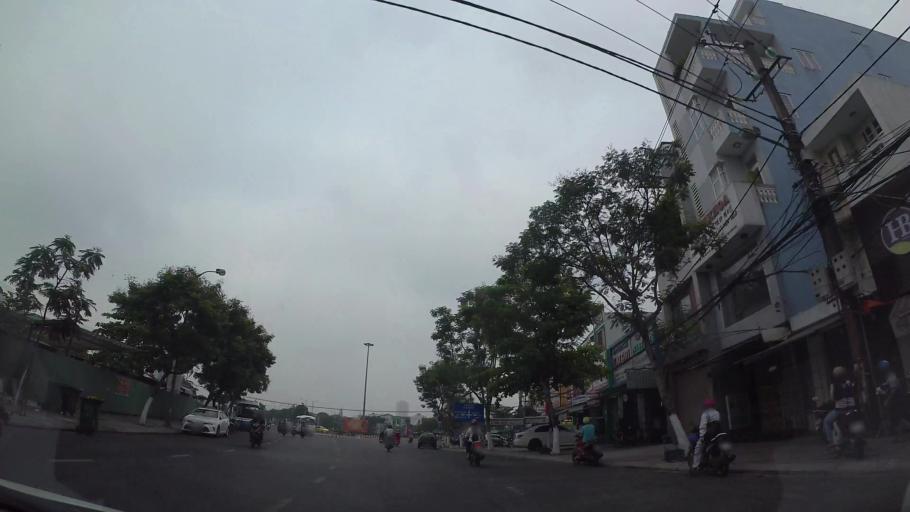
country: VN
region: Da Nang
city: Son Tra
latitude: 16.0549
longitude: 108.2381
